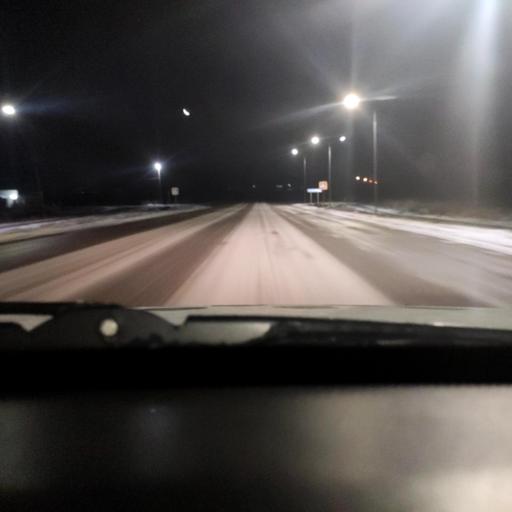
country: RU
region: Perm
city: Kultayevo
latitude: 57.8692
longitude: 55.8702
